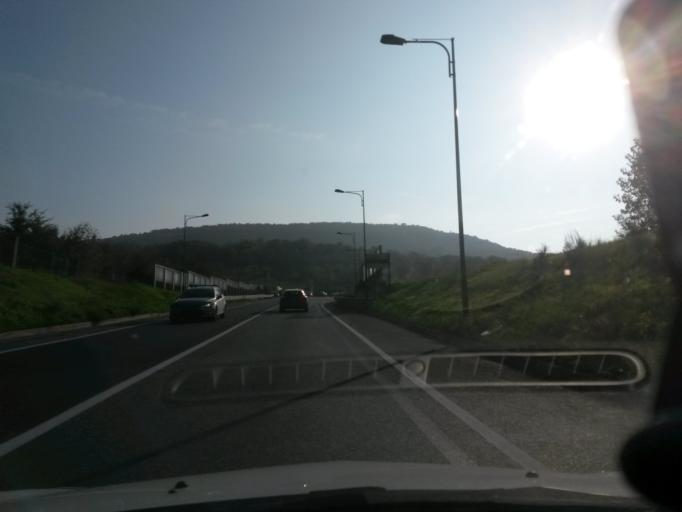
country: IT
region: Piedmont
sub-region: Provincia di Torino
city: Ferriera
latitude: 45.0754
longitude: 7.4143
